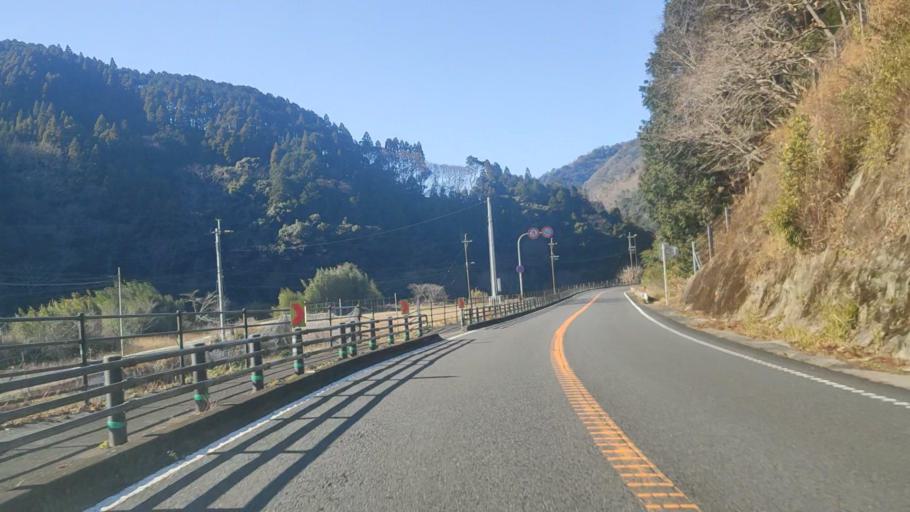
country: JP
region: Oita
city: Usuki
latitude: 33.0033
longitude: 131.7439
